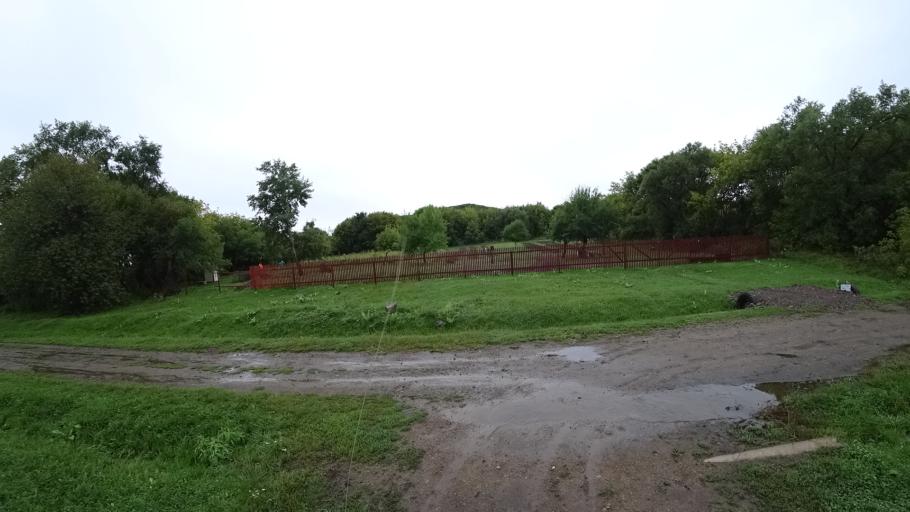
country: RU
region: Primorskiy
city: Monastyrishche
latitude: 44.2502
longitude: 132.4232
